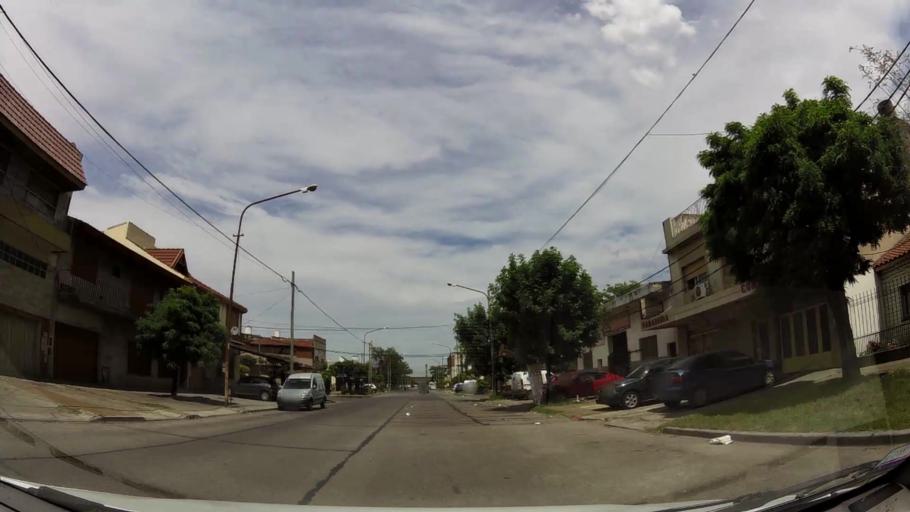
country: AR
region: Buenos Aires
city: San Justo
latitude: -34.6842
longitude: -58.5464
